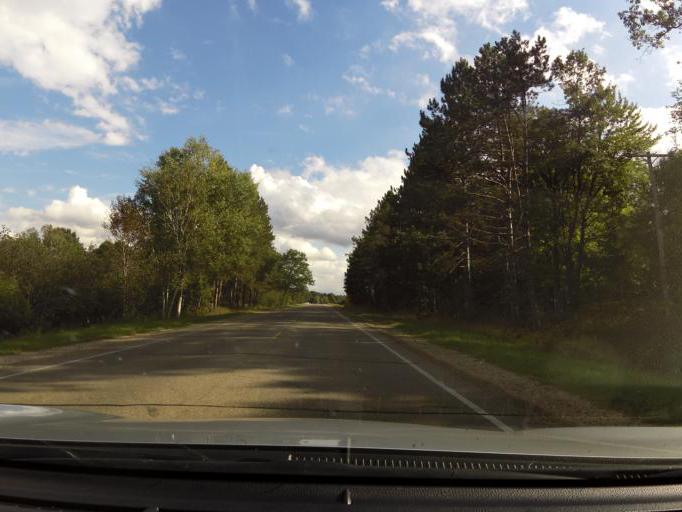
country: US
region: Michigan
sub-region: Roscommon County
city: Saint Helen
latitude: 44.3855
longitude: -84.4277
